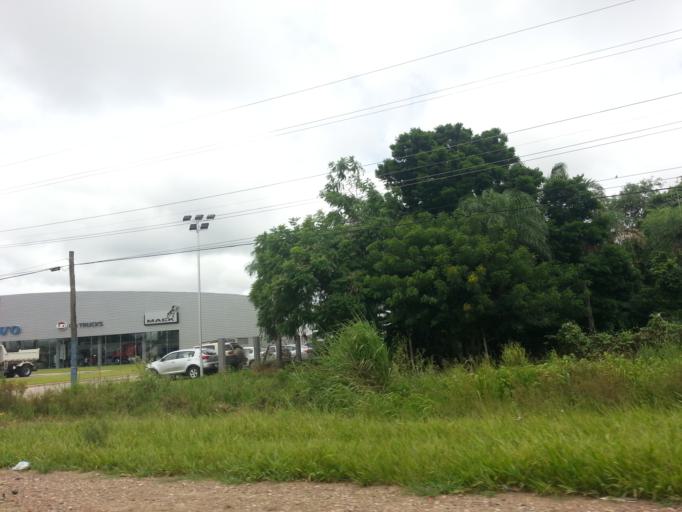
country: BO
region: Santa Cruz
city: La Belgica
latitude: -17.6532
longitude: -63.1579
